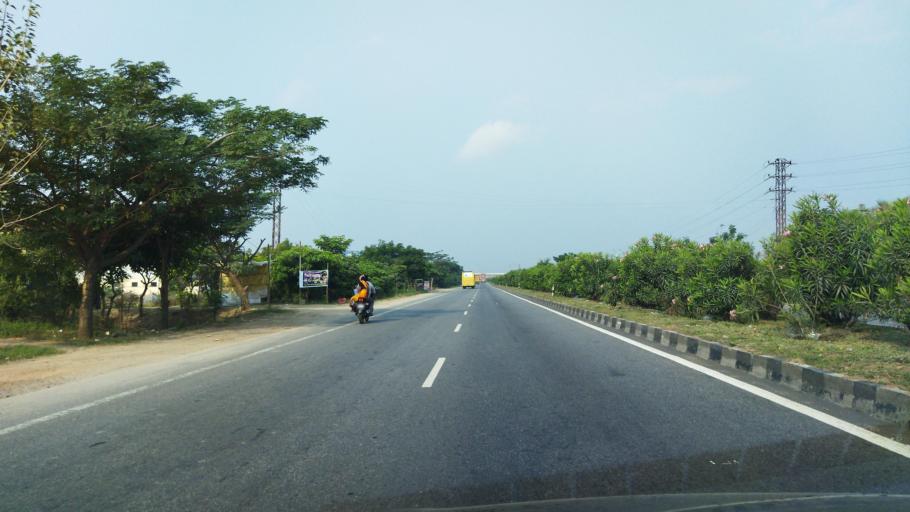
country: IN
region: Telangana
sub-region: Nalgonda
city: Nalgonda
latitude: 17.1680
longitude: 79.4020
